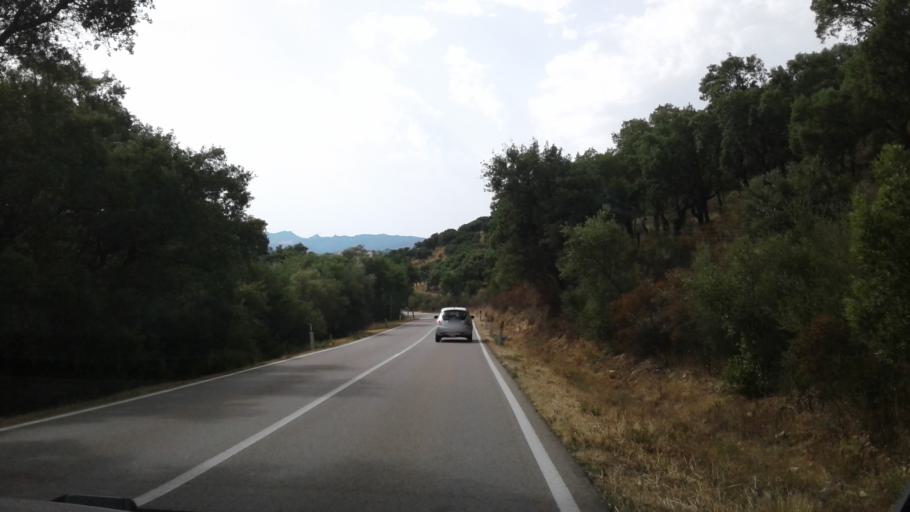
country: IT
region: Sardinia
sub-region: Provincia di Olbia-Tempio
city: Sant'Antonio di Gallura
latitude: 40.9608
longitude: 9.2902
